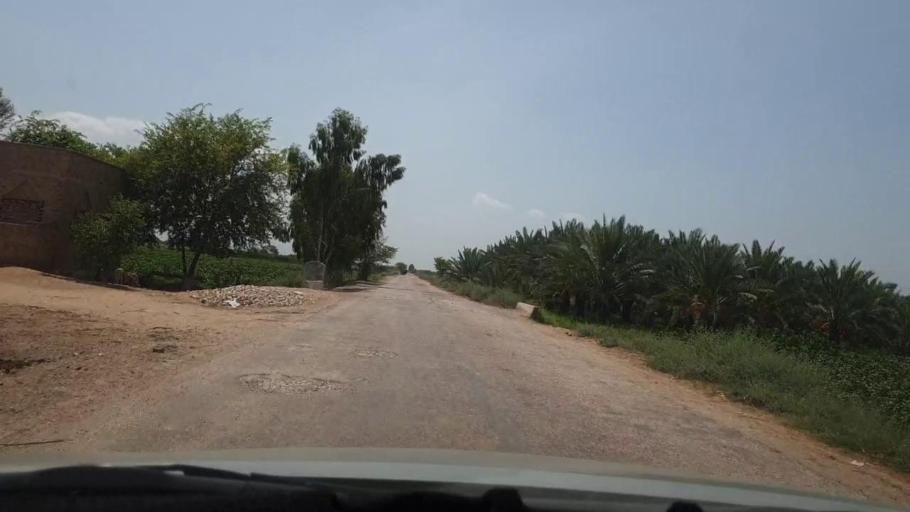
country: PK
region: Sindh
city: Rohri
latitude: 27.6696
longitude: 69.0752
